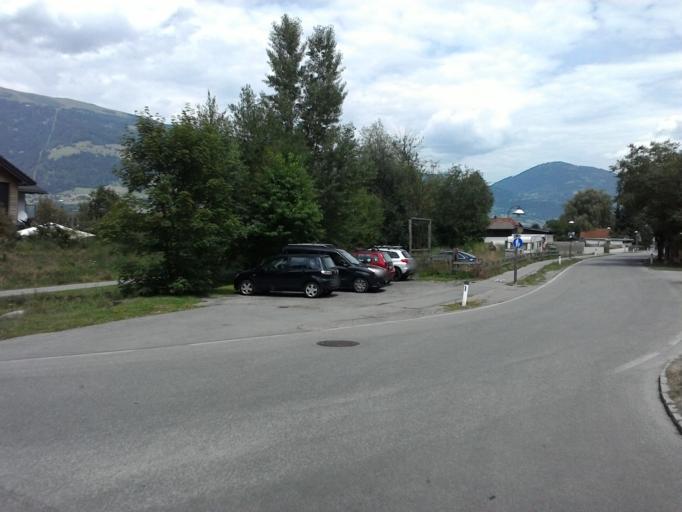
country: AT
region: Tyrol
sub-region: Politischer Bezirk Lienz
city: Amlach
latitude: 46.8135
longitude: 12.7626
